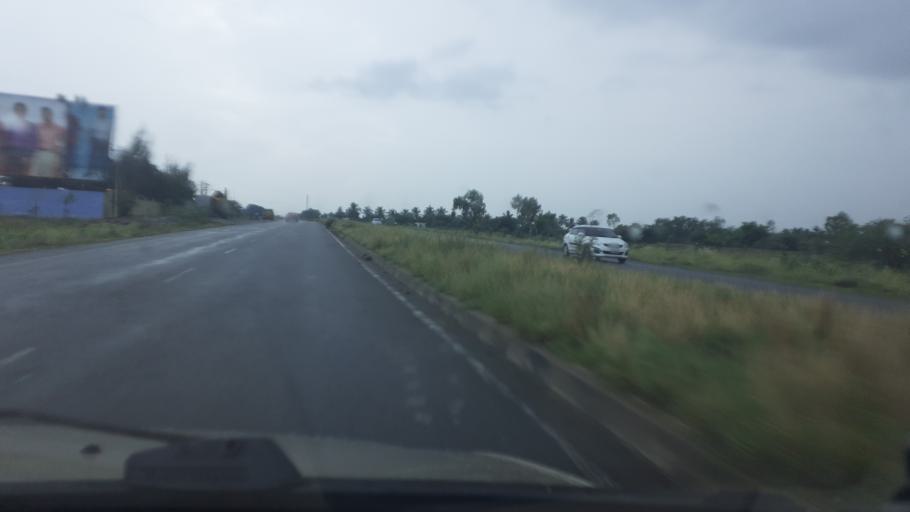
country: IN
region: Tamil Nadu
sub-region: Thoothukkudi
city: Kadambur
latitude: 9.0278
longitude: 77.7885
